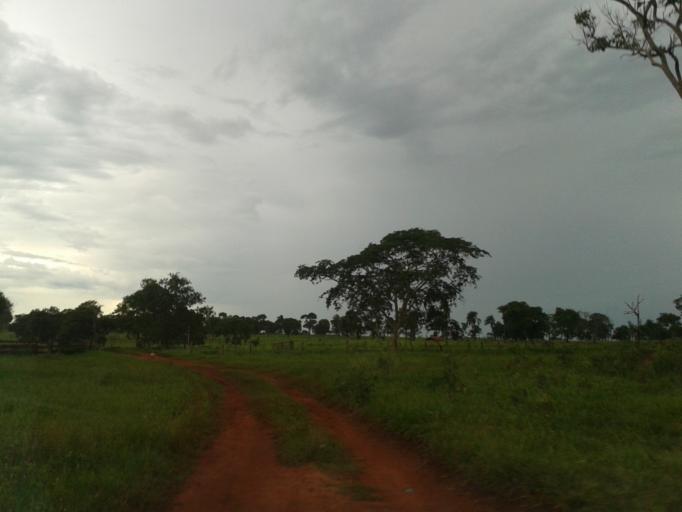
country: BR
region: Minas Gerais
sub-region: Santa Vitoria
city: Santa Vitoria
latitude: -19.2030
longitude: -50.5155
